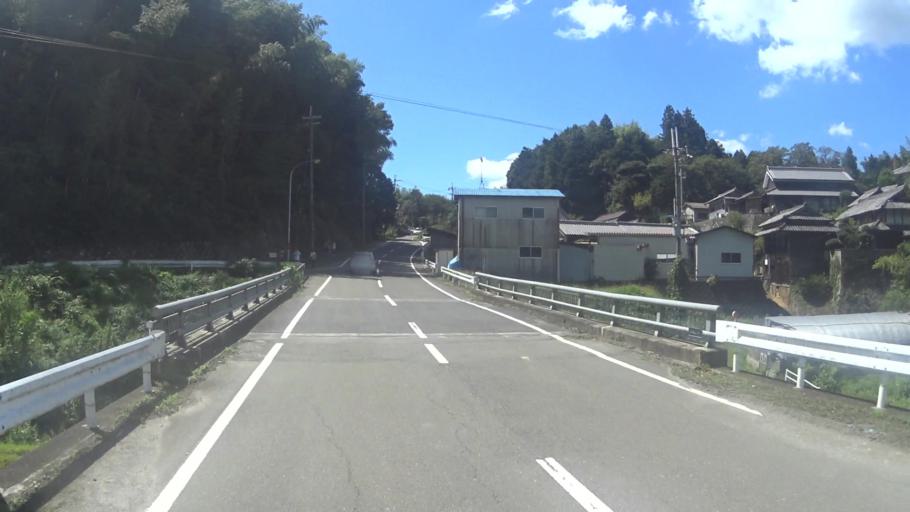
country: JP
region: Nara
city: Nara-shi
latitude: 34.7191
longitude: 135.8769
